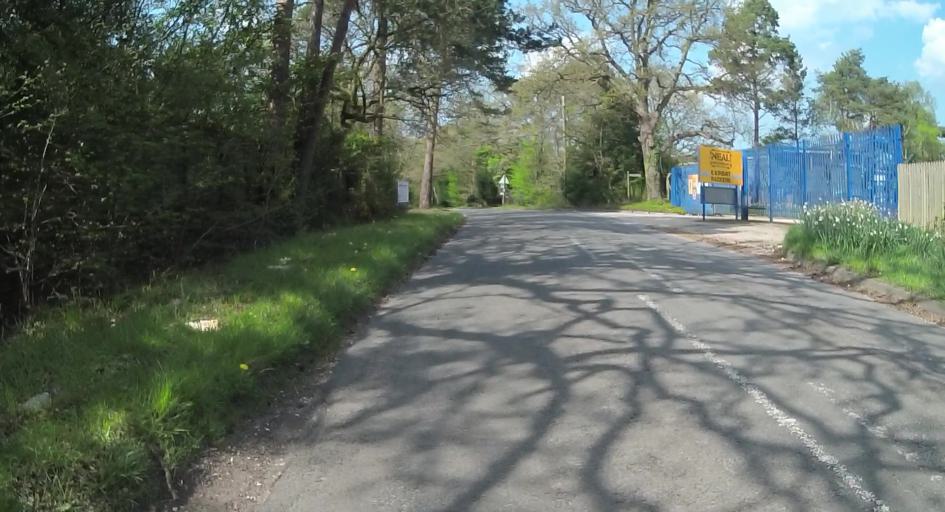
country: GB
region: England
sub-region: Hampshire
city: Tadley
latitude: 51.3667
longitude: -1.1188
